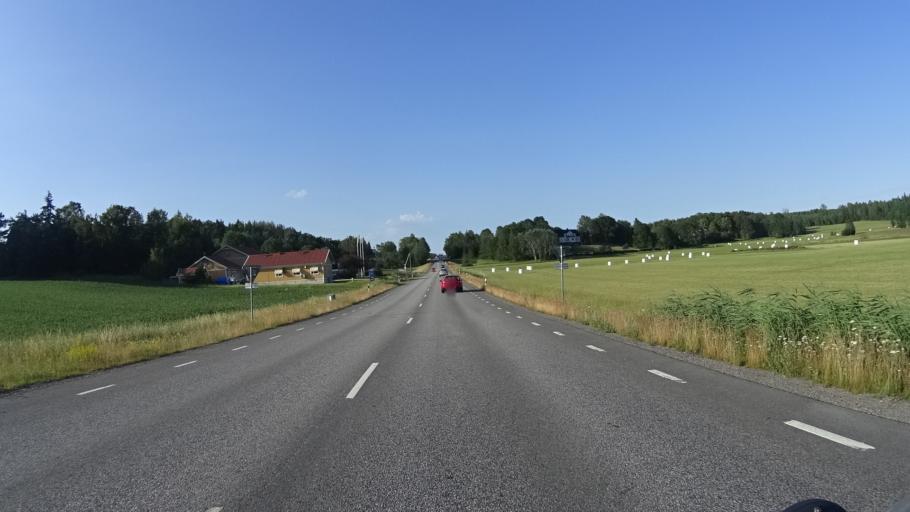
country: SE
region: Stockholm
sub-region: Sodertalje Kommun
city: Pershagen
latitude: 59.0855
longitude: 17.6093
